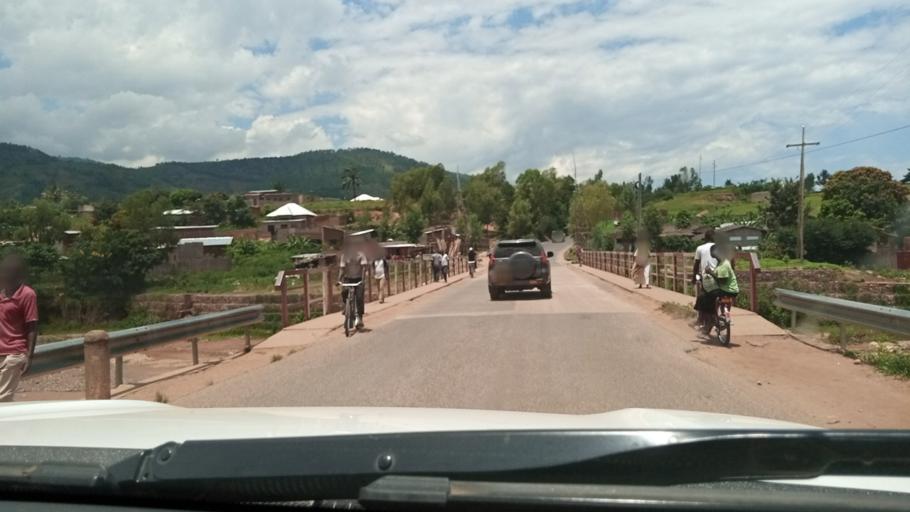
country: BI
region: Bujumbura Mairie
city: Bujumbura
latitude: -3.4799
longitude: 29.3532
